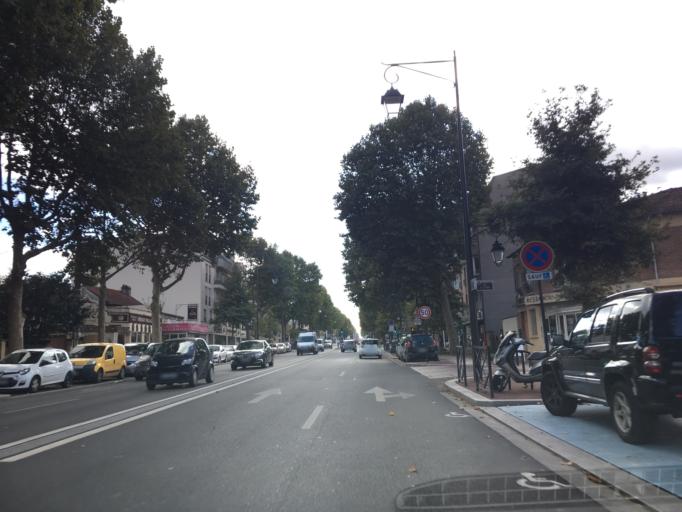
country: FR
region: Ile-de-France
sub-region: Departement des Hauts-de-Seine
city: Antony
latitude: 48.7471
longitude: 2.3037
